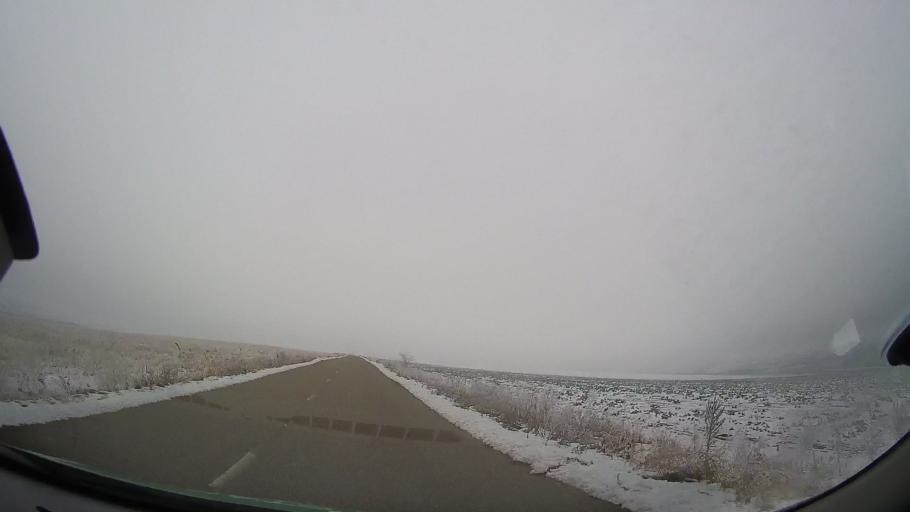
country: RO
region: Vaslui
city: Coroiesti
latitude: 46.2150
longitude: 27.4809
